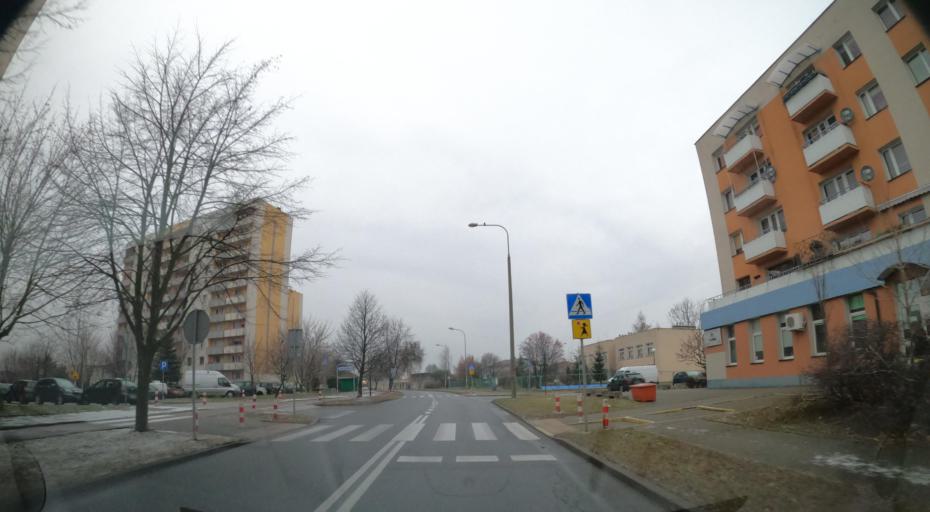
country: PL
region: Masovian Voivodeship
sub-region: Powiat radomski
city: Trablice
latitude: 51.3723
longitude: 21.1305
